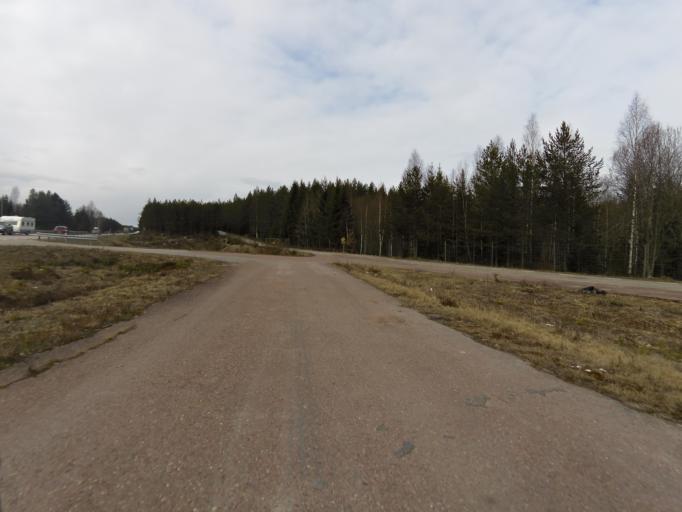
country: SE
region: Gaevleborg
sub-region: Hofors Kommun
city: Hofors
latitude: 60.5410
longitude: 16.1845
